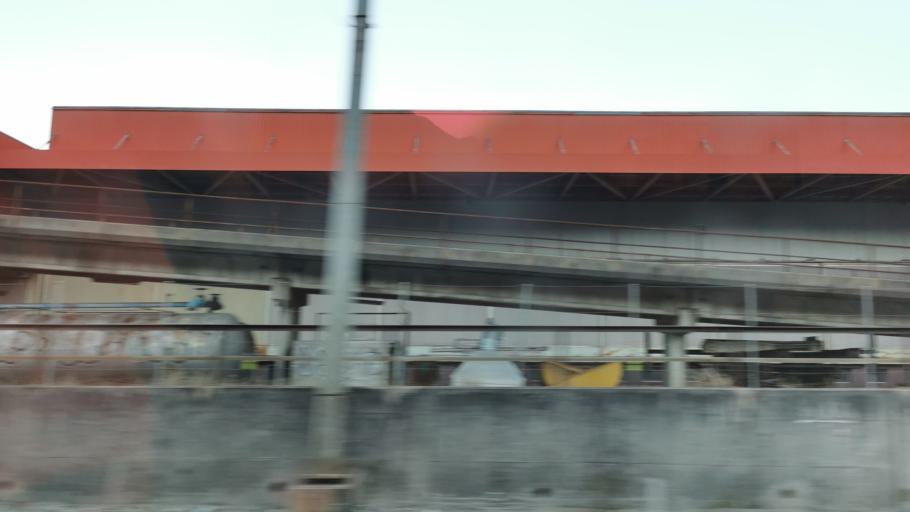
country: CH
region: Ticino
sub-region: Bellinzona District
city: Giubiasco
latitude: 46.1769
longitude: 9.0082
